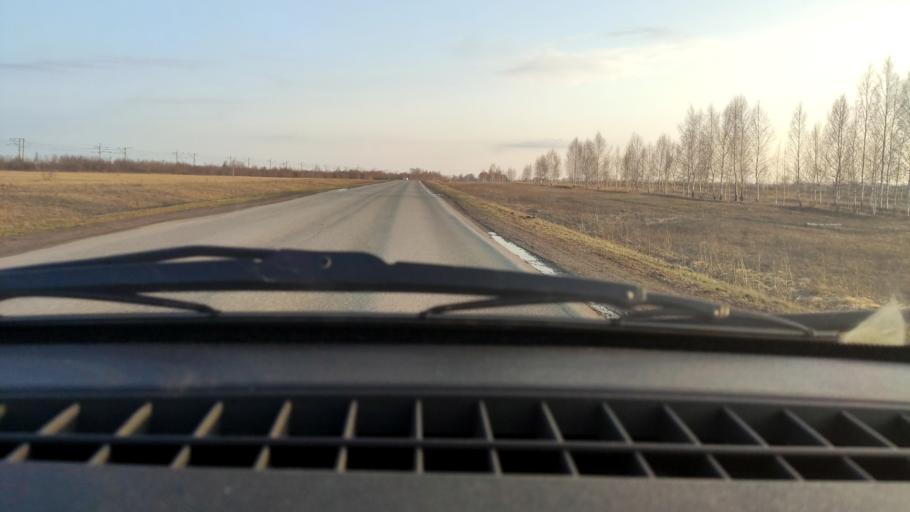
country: RU
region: Bashkortostan
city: Chishmy
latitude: 54.4335
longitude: 55.2353
